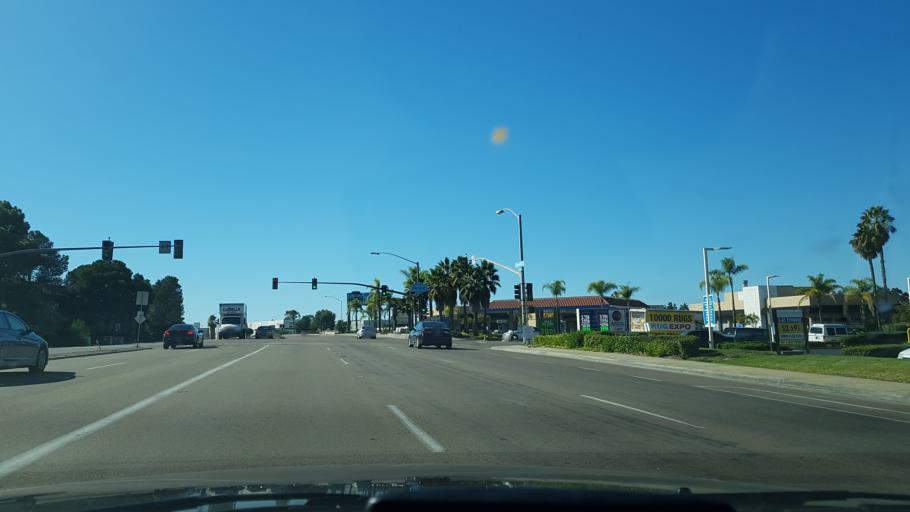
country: US
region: California
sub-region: San Diego County
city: La Jolla
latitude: 32.8777
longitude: -117.1717
